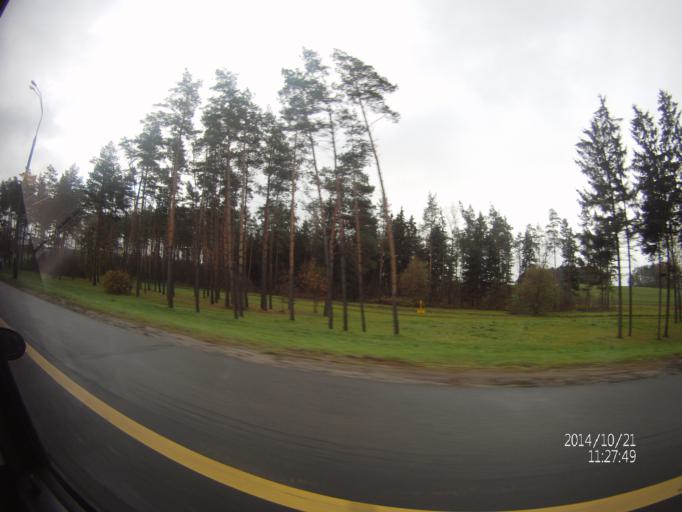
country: BY
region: Minsk
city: Syomkava
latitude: 53.9675
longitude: 27.4910
